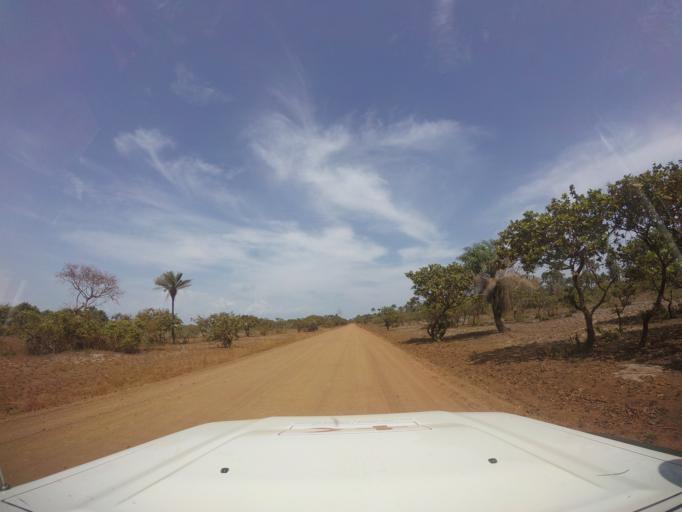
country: LR
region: Grand Cape Mount
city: Robertsport
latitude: 6.7031
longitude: -11.3159
